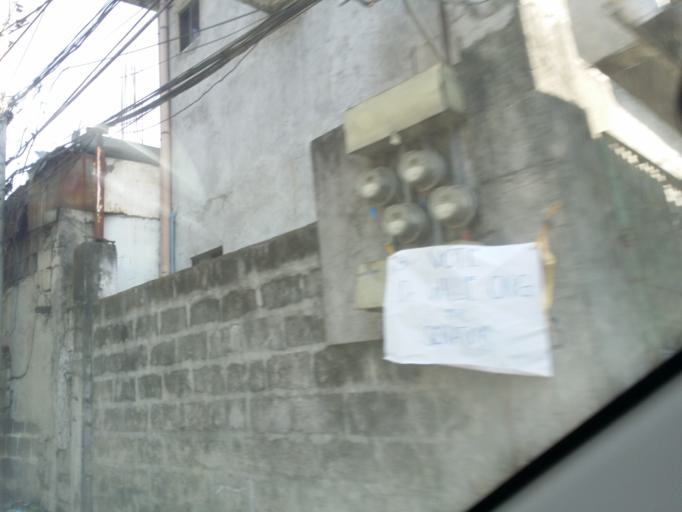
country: PH
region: Metro Manila
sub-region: Mandaluyong
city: Mandaluyong City
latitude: 14.5777
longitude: 121.0223
